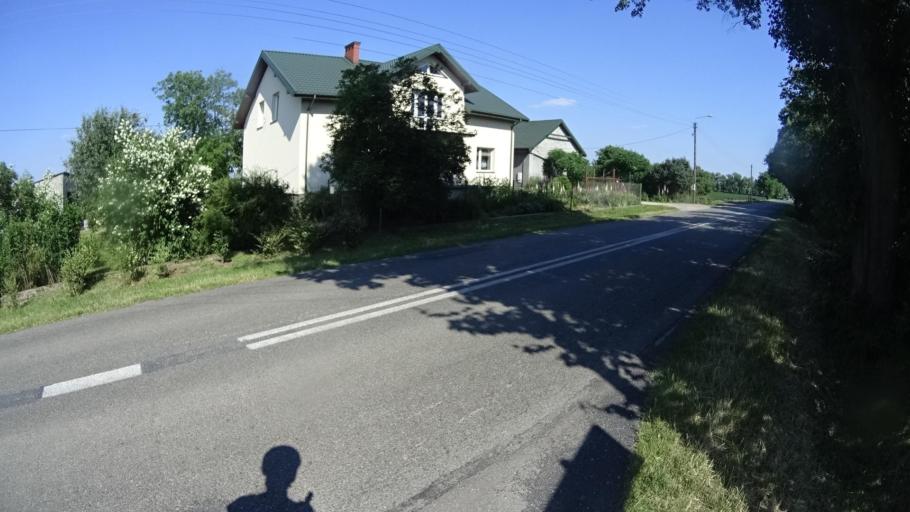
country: PL
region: Masovian Voivodeship
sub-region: Powiat warszawski zachodni
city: Jozefow
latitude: 52.1639
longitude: 20.6657
